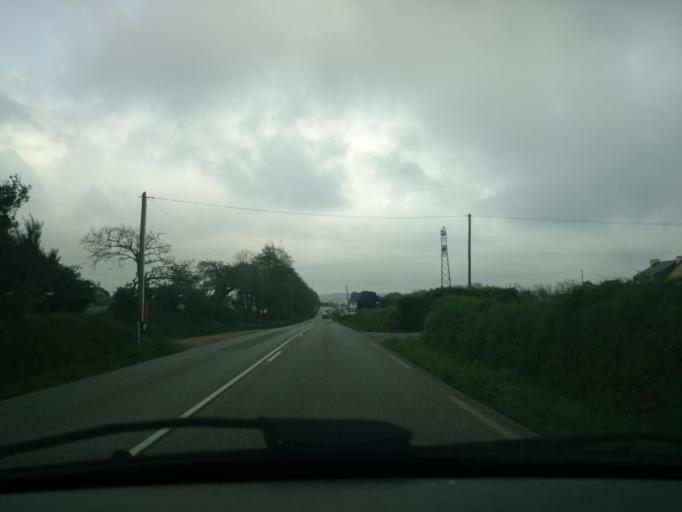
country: FR
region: Brittany
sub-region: Departement du Finistere
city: Saint-Renan
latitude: 48.4530
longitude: -4.6245
